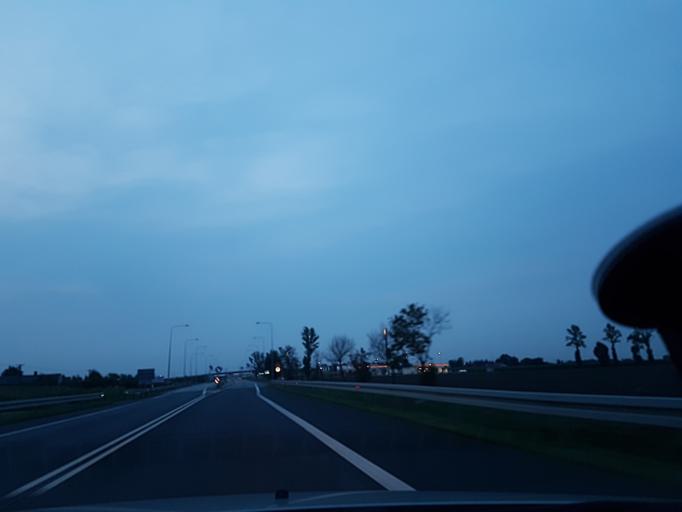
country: PL
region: Lodz Voivodeship
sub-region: Powiat kutnowski
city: Krzyzanow
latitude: 52.2203
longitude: 19.4579
